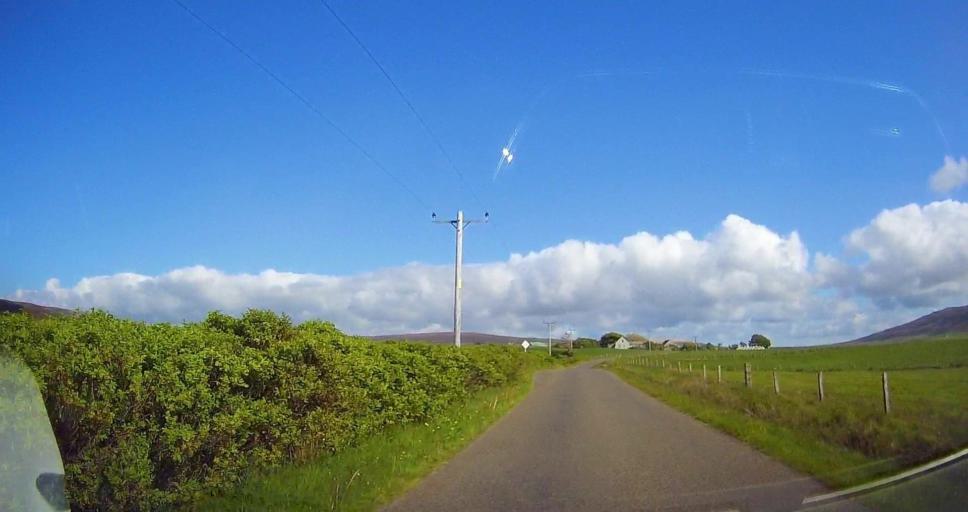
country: GB
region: Scotland
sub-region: Orkney Islands
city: Stromness
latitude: 58.9960
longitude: -3.1621
